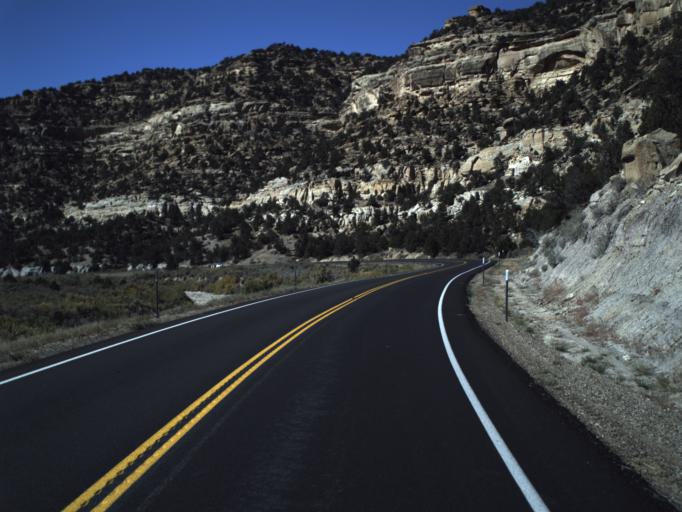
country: US
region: Utah
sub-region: Wayne County
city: Loa
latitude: 37.7406
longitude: -111.7178
